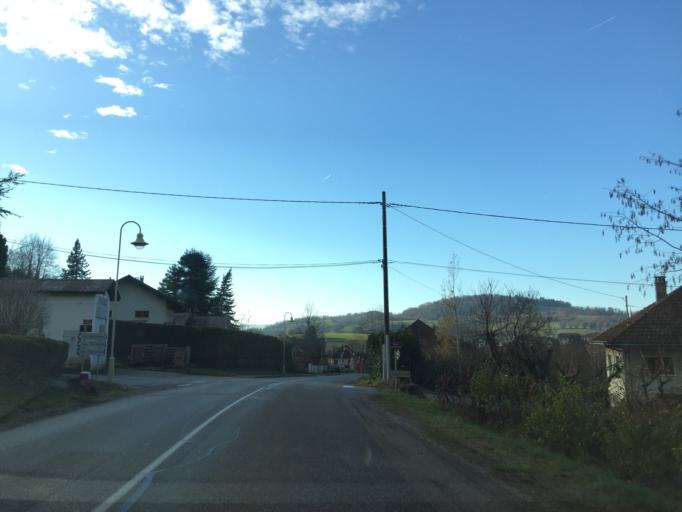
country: FR
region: Rhone-Alpes
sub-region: Departement de la Haute-Savoie
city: Cusy
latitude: 45.7651
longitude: 6.0357
